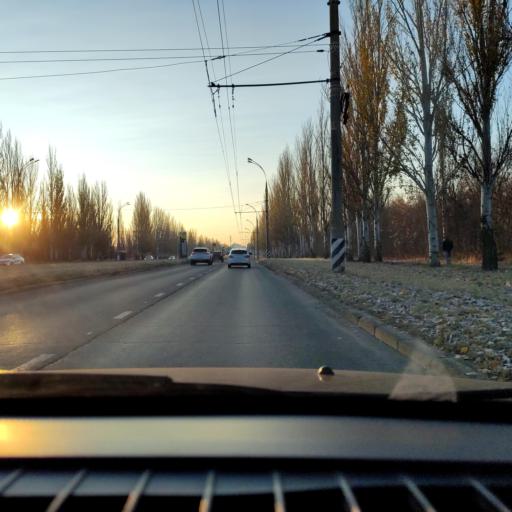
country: RU
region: Samara
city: Tol'yatti
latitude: 53.5496
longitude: 49.2711
